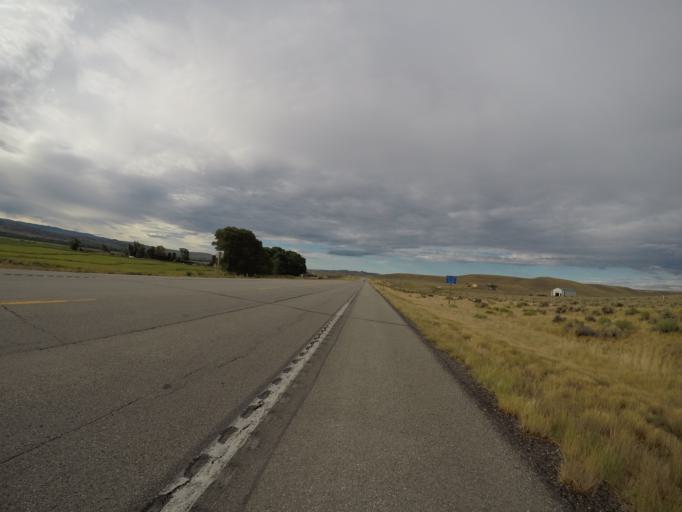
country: US
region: Wyoming
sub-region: Carbon County
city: Saratoga
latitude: 41.3752
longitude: -106.7478
